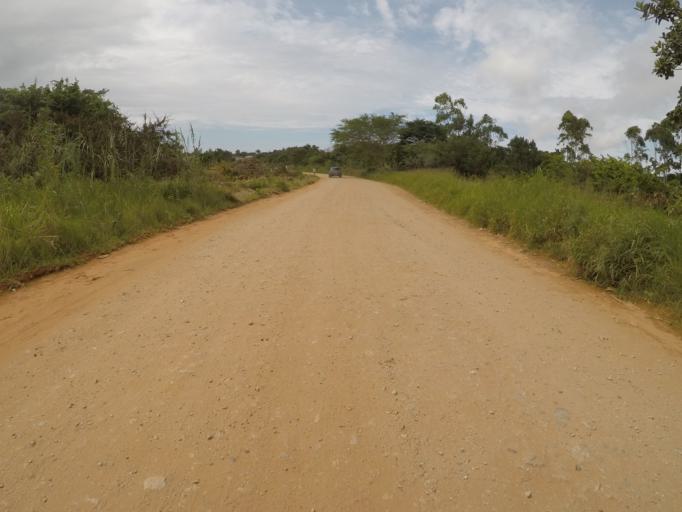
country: ZA
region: KwaZulu-Natal
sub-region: uThungulu District Municipality
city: eSikhawini
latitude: -28.8575
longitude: 31.9159
